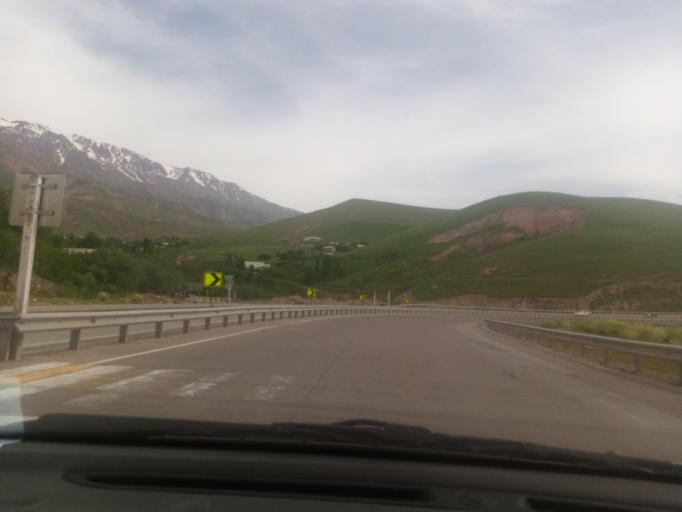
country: UZ
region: Toshkent
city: Angren
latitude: 41.0669
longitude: 70.2201
